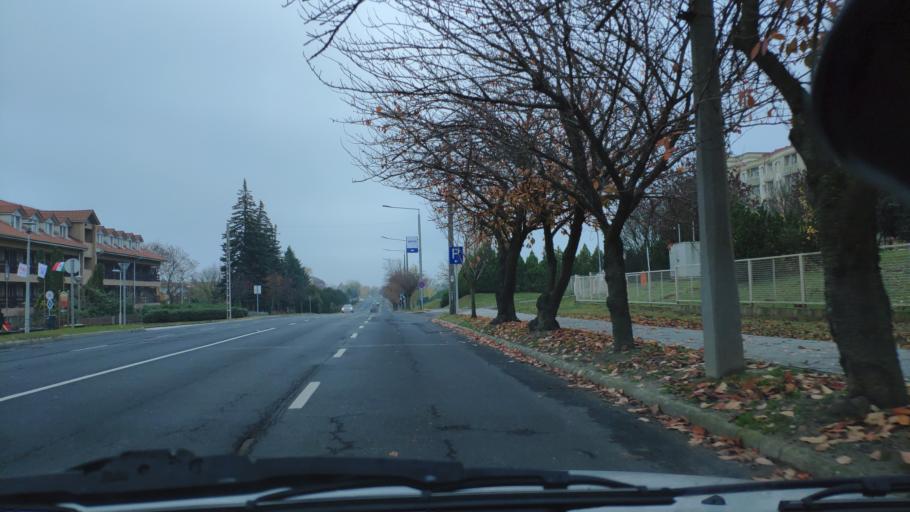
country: HU
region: Zala
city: Zalakomar
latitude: 46.5473
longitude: 17.1245
